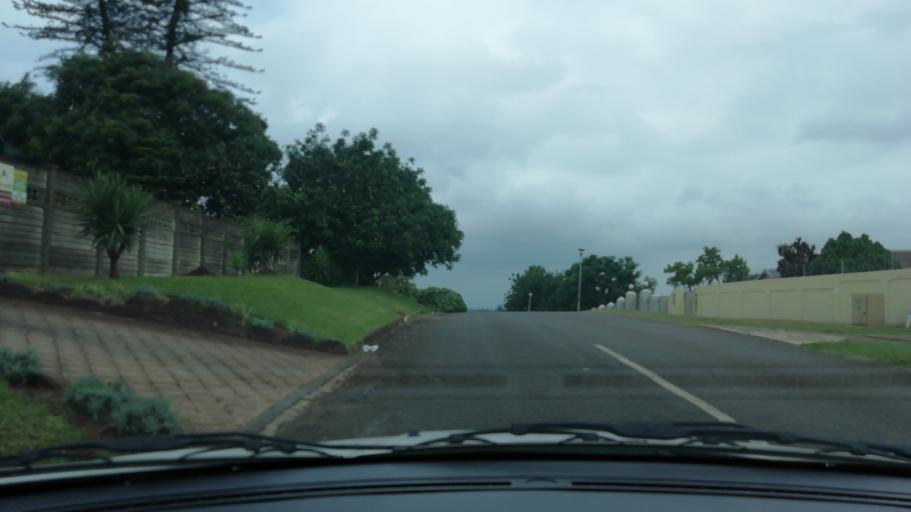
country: ZA
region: KwaZulu-Natal
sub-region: uThungulu District Municipality
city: Empangeni
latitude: -28.7375
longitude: 31.8987
